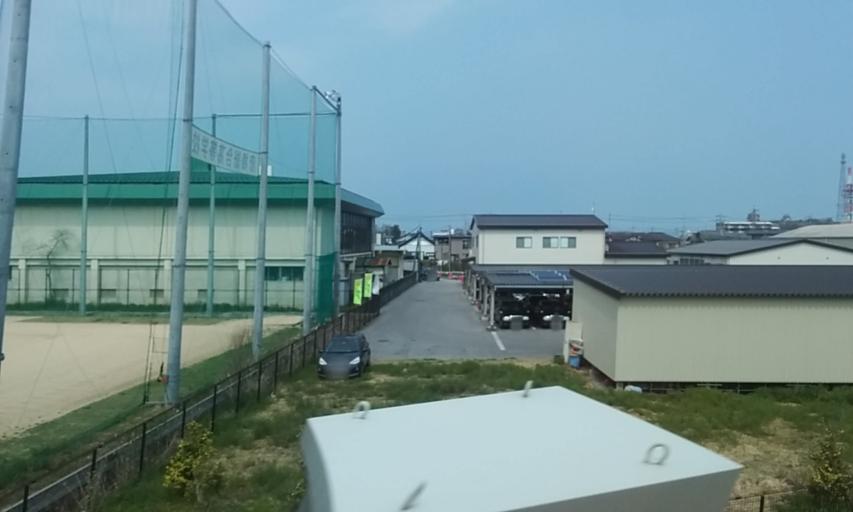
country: JP
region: Shiga Prefecture
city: Hikone
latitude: 35.2636
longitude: 136.2614
